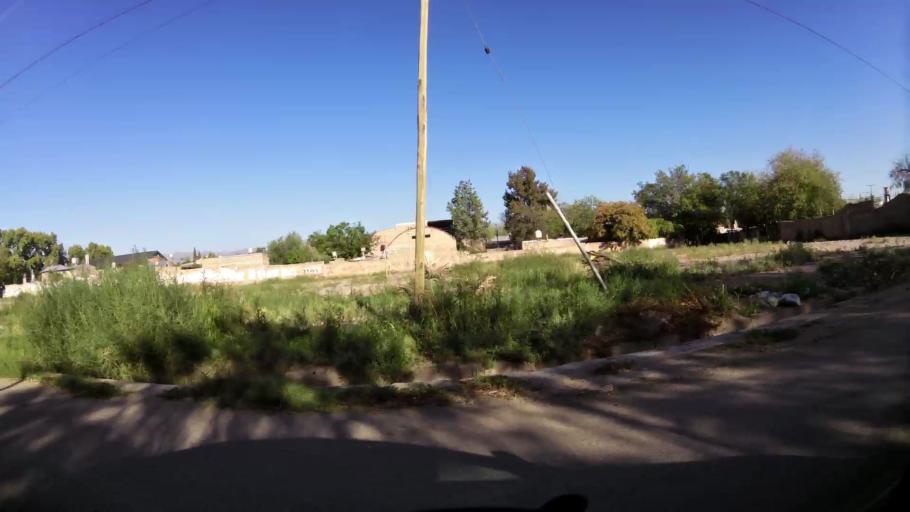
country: AR
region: Mendoza
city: Las Heras
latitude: -32.8576
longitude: -68.8194
